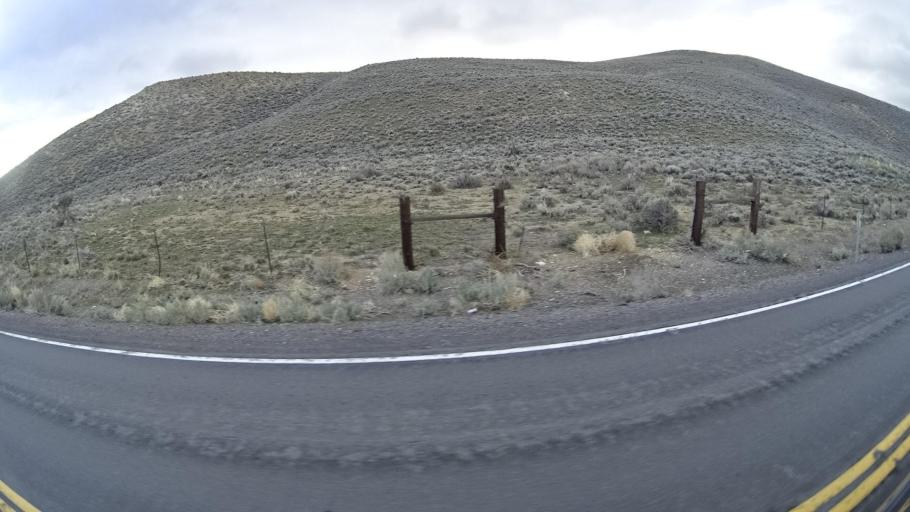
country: US
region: Nevada
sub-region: Carson City
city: Carson City
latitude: 39.2245
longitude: -119.7966
